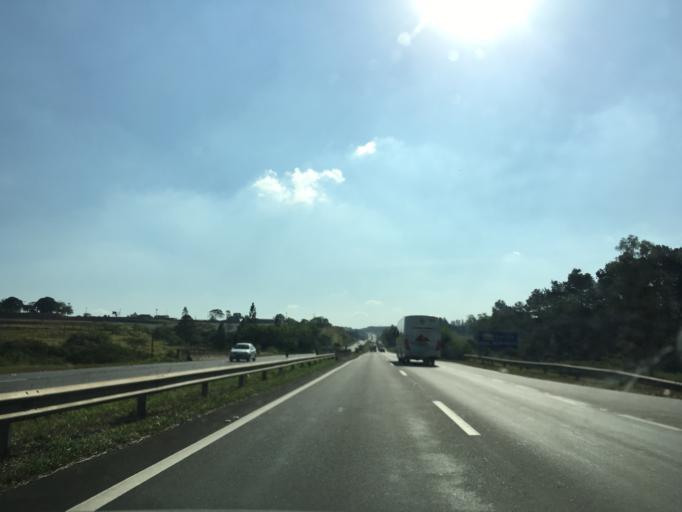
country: BR
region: Sao Paulo
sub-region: Santa Barbara D'Oeste
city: Santa Barbara d'Oeste
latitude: -22.7387
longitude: -47.5272
